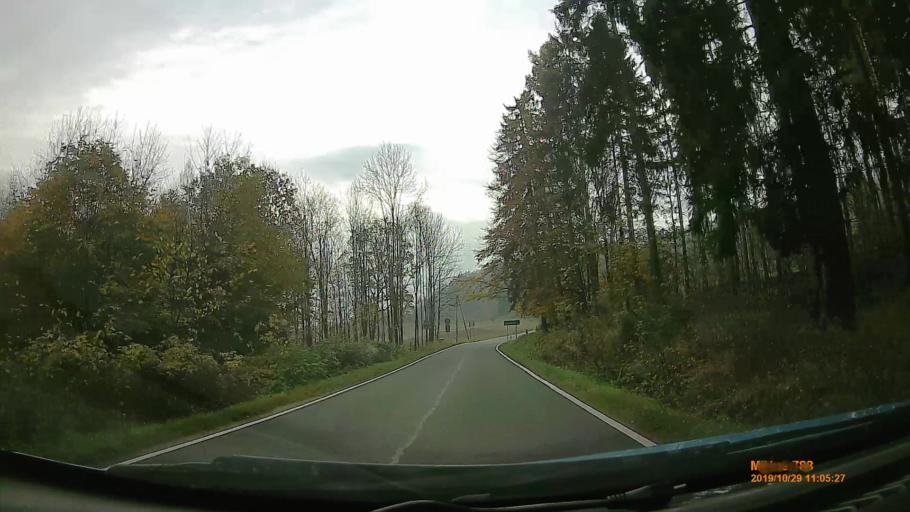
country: PL
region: Lower Silesian Voivodeship
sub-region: Powiat klodzki
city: Szczytna
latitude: 50.4706
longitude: 16.4758
